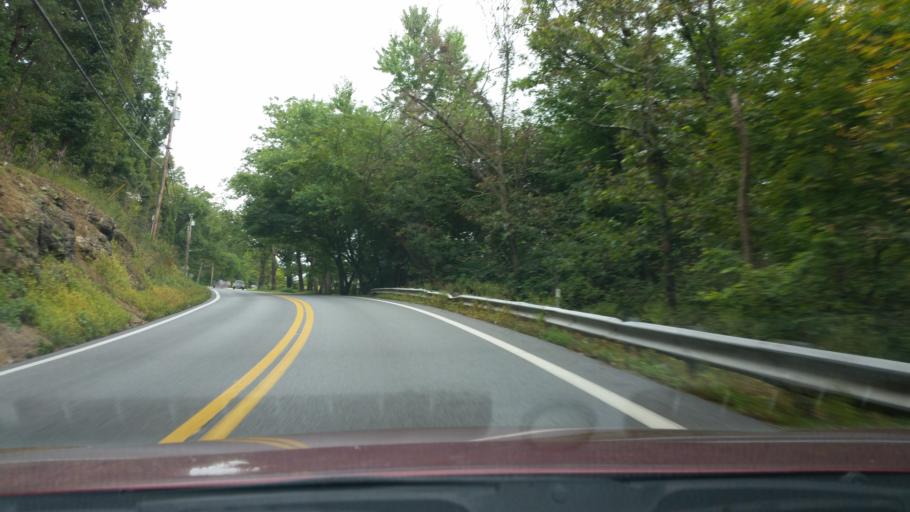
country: US
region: West Virginia
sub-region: Berkeley County
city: Martinsburg
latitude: 39.5878
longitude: -78.0592
